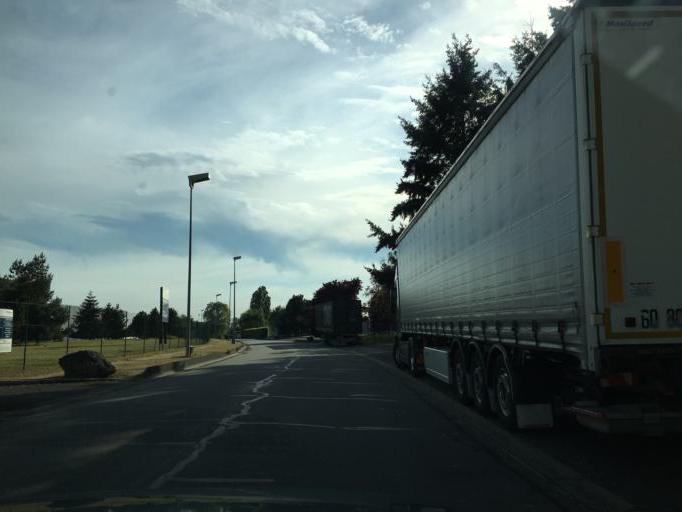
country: FR
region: Centre
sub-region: Departement du Loiret
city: Ormes
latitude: 47.9485
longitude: 1.8359
